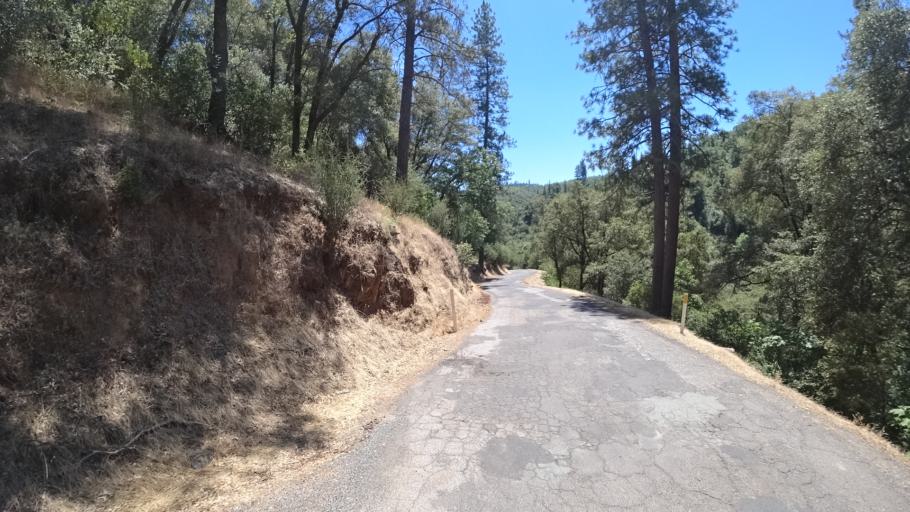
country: US
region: California
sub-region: Calaveras County
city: Forest Meadows
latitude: 38.2058
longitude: -120.4549
